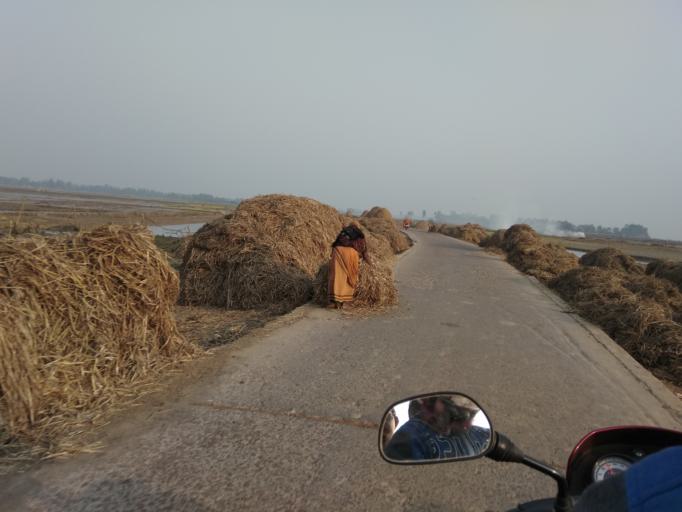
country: BD
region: Rajshahi
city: Ishurdi
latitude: 24.4799
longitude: 89.2381
